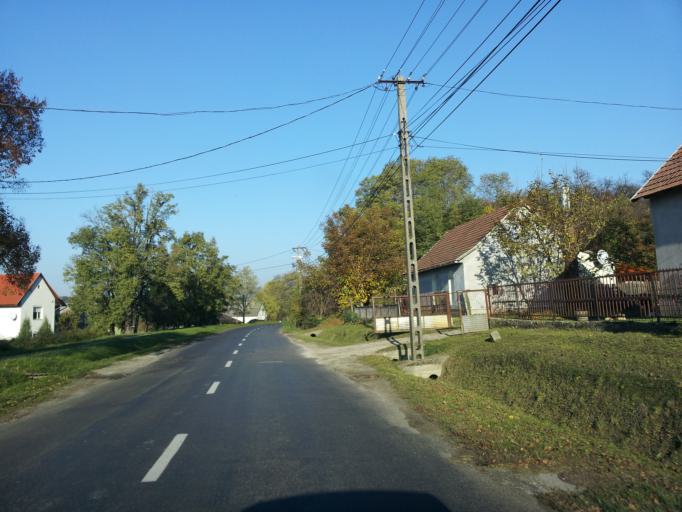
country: HU
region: Fejer
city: Bodajk
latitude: 47.3135
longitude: 18.1934
